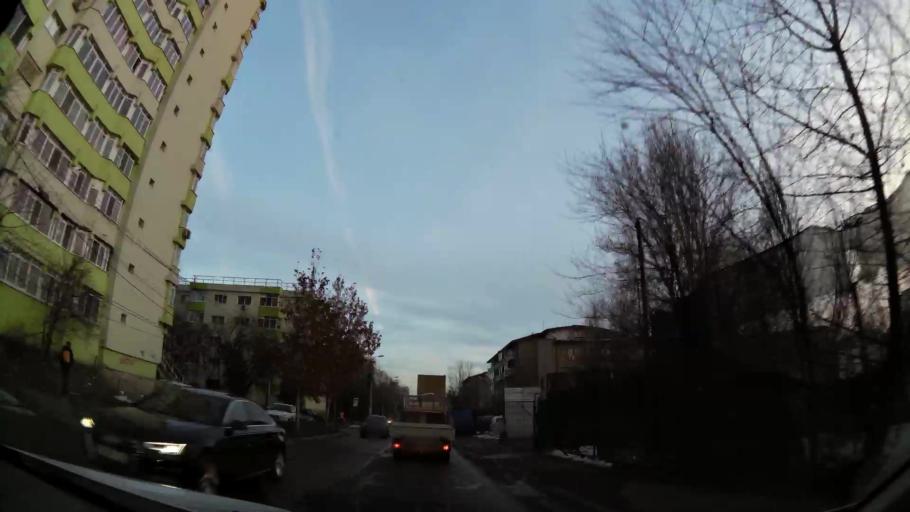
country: RO
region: Ilfov
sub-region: Comuna Fundeni-Dobroesti
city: Fundeni
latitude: 44.4654
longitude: 26.1392
